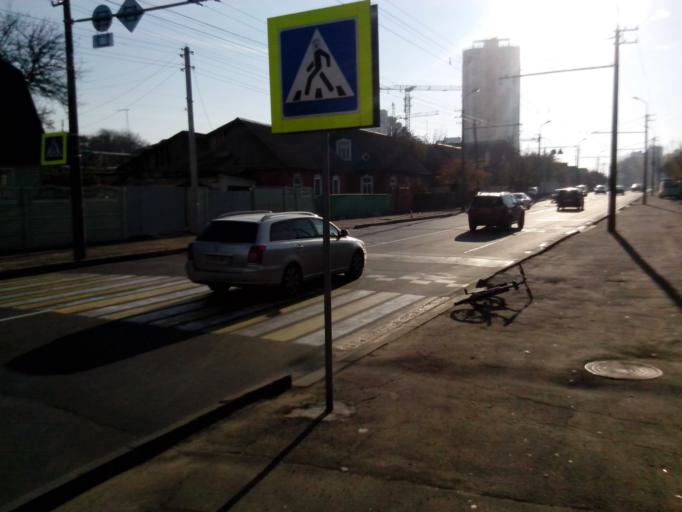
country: BY
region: Minsk
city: Minsk
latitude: 53.9424
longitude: 27.5878
